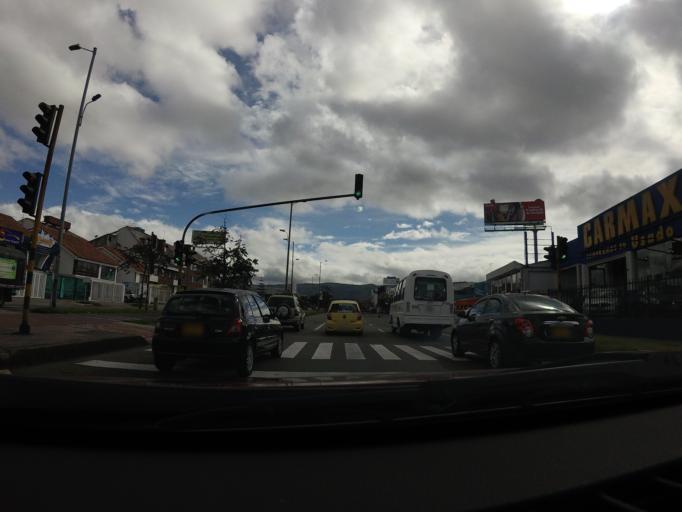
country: CO
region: Bogota D.C.
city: Barrio San Luis
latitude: 4.7105
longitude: -74.0739
